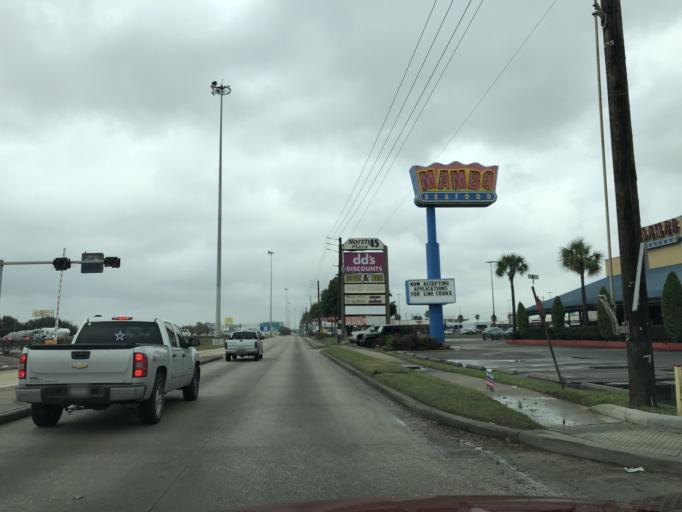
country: US
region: Texas
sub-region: Harris County
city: Aldine
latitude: 29.9216
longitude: -95.4120
